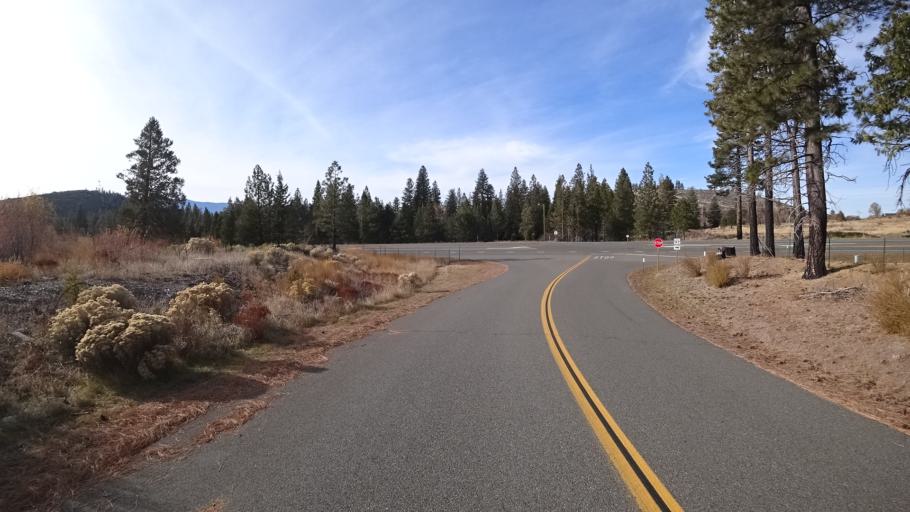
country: US
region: California
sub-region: Siskiyou County
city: Weed
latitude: 41.4401
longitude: -122.3855
